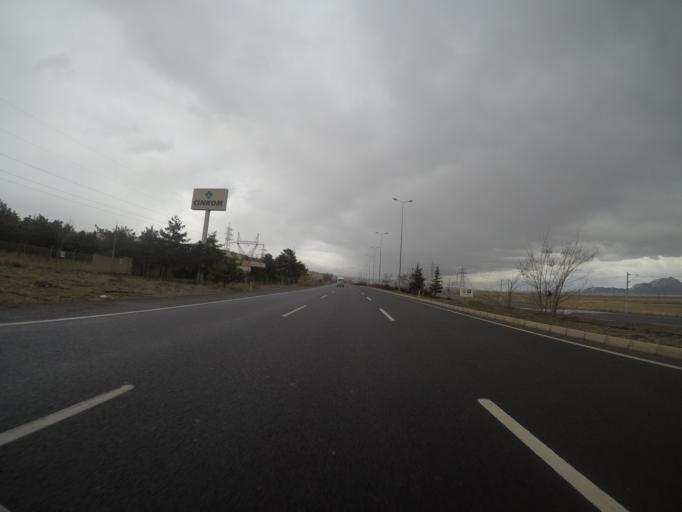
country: TR
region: Kayseri
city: Incesu
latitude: 38.7157
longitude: 35.2675
